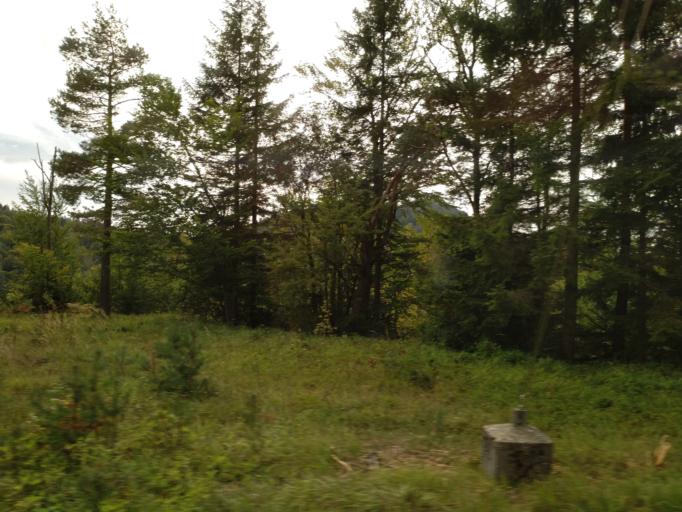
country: AT
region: Lower Austria
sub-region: Politischer Bezirk Lilienfeld
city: Mitterbach am Erlaufsee
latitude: 47.8686
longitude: 15.3072
